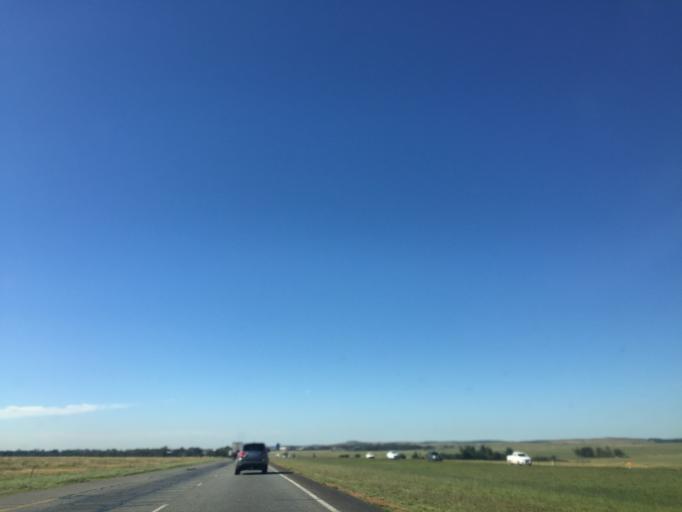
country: ZA
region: Gauteng
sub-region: Ekurhuleni Metropolitan Municipality
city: Germiston
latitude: -26.3879
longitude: 28.0857
